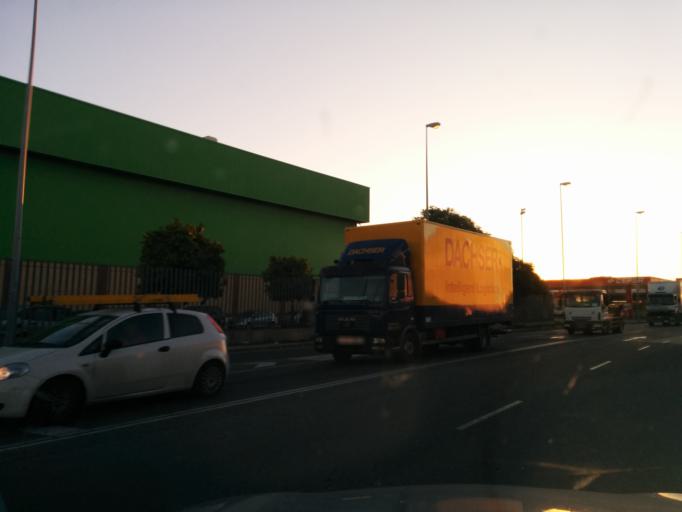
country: ES
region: Andalusia
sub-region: Provincia de Sevilla
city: Sevilla
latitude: 37.3814
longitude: -5.9388
